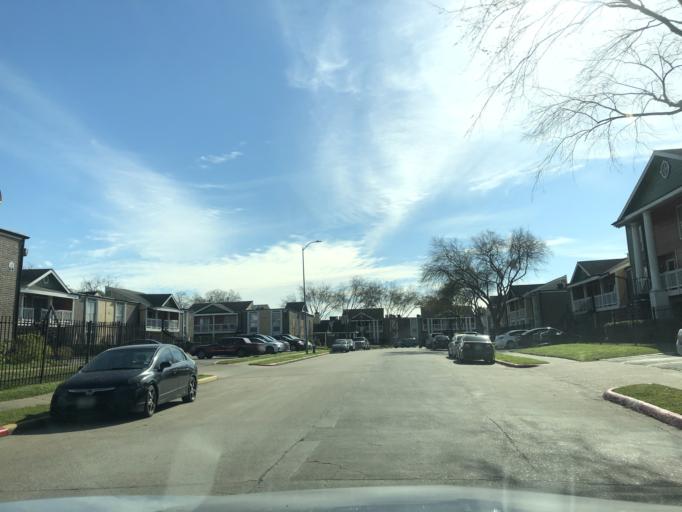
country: US
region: Texas
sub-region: Harris County
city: Bellaire
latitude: 29.6798
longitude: -95.5058
